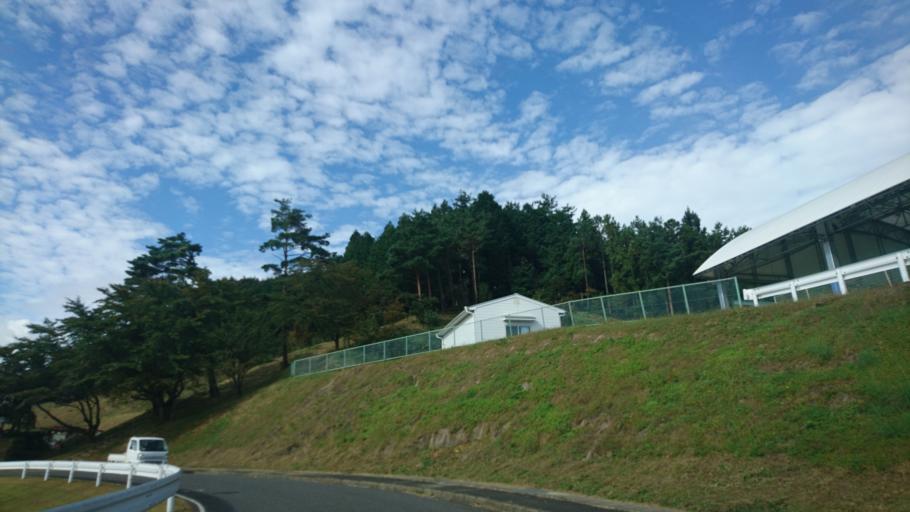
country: JP
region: Fukushima
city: Sukagawa
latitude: 37.3077
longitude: 140.2696
